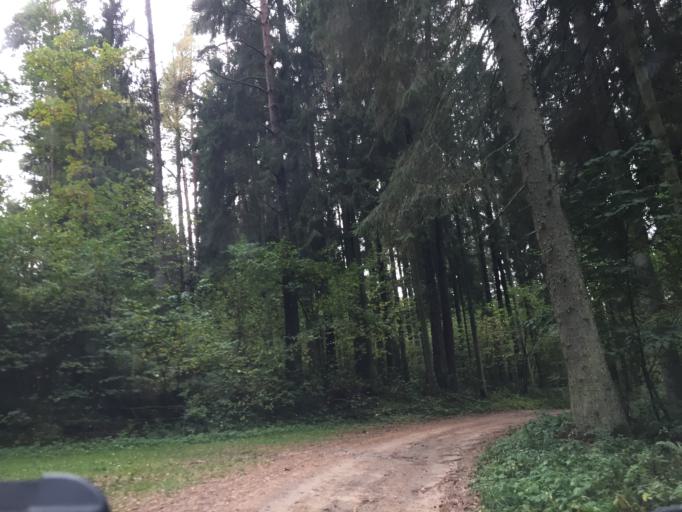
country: LV
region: Auces Novads
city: Auce
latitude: 56.5482
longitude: 23.0402
